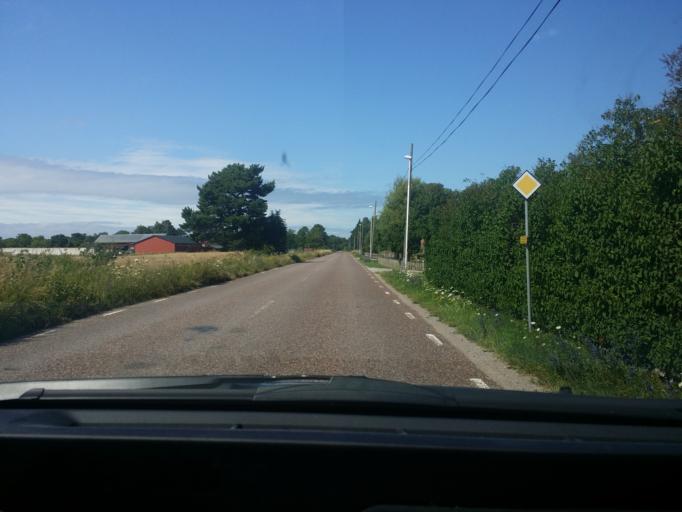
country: SE
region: Kalmar
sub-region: Borgholms Kommun
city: Borgholm
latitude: 57.2060
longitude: 16.9768
